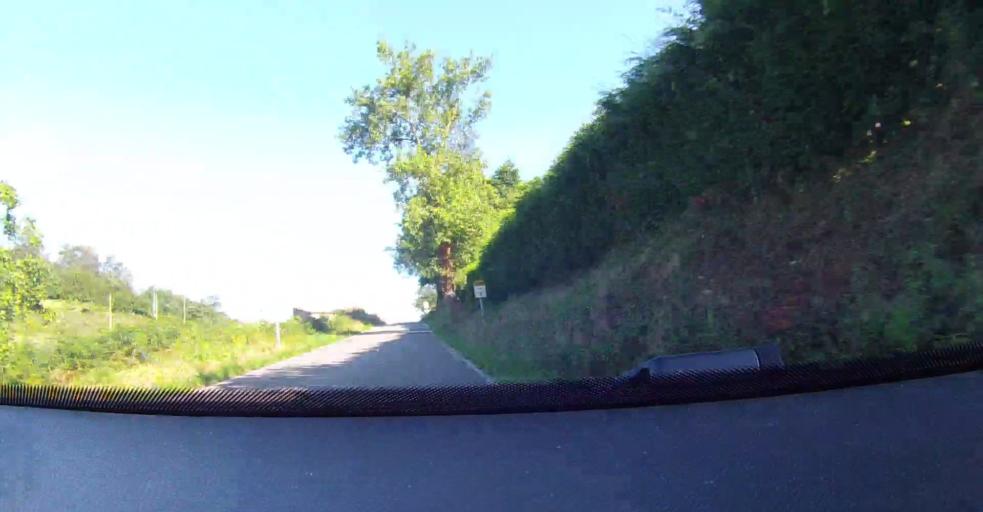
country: ES
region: Asturias
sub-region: Province of Asturias
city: Villaviciosa
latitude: 43.4852
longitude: -5.4082
